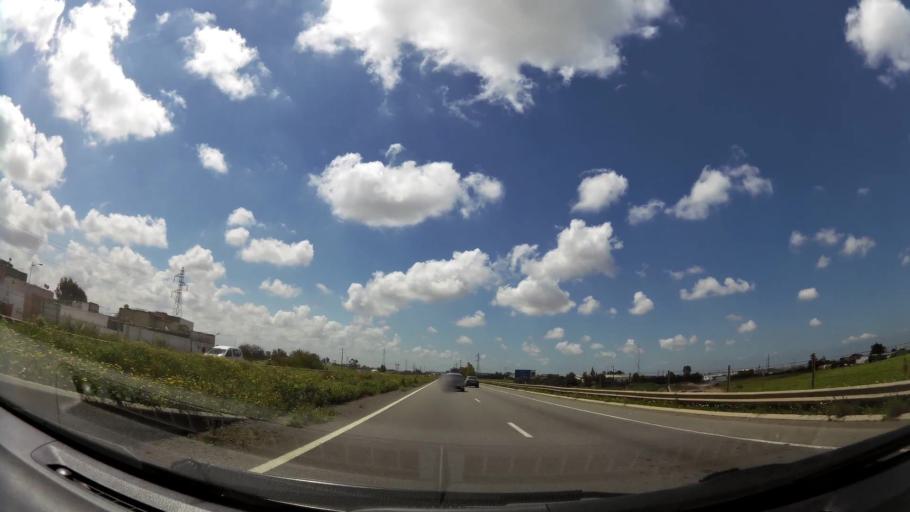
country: MA
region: Grand Casablanca
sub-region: Casablanca
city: Casablanca
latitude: 33.5154
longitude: -7.5932
